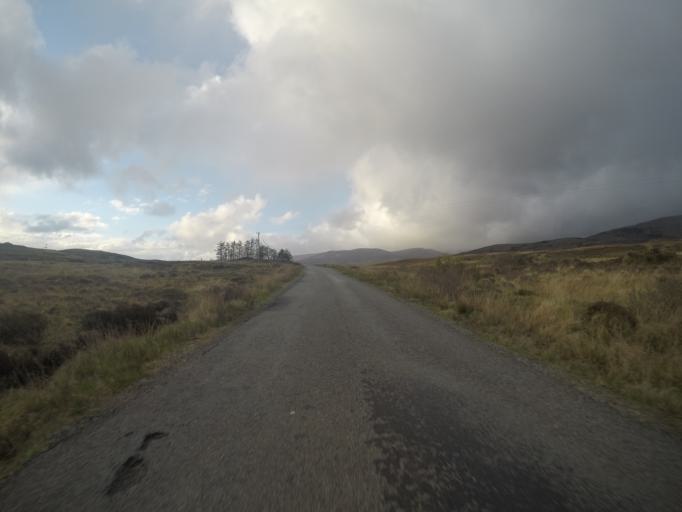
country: GB
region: Scotland
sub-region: Highland
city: Isle of Skye
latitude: 57.4575
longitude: -6.2971
